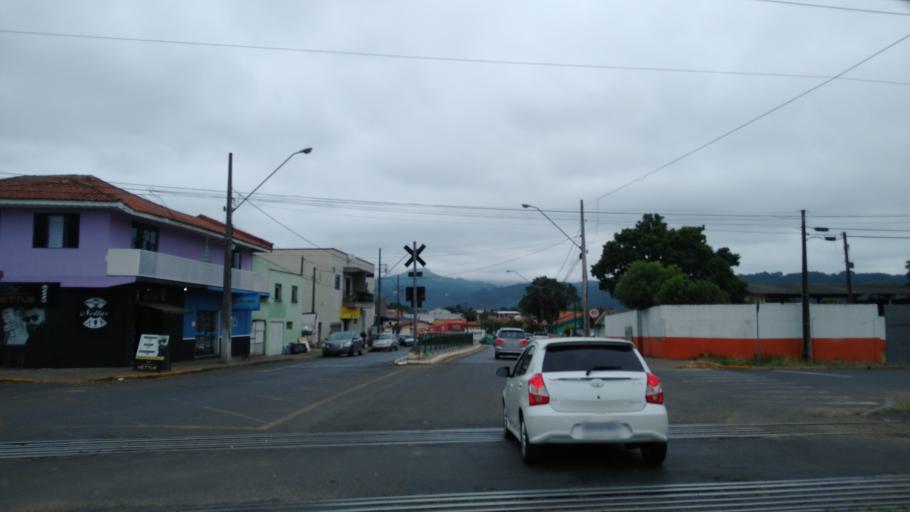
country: BR
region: Santa Catarina
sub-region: Porto Uniao
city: Porto Uniao
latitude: -26.2501
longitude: -51.0842
